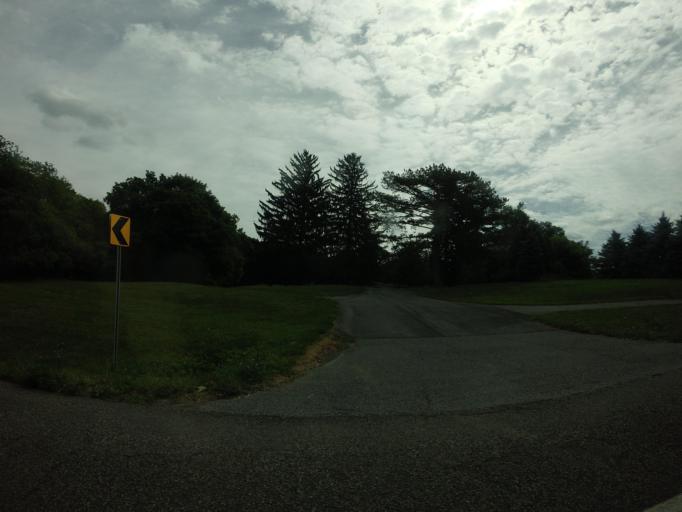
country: US
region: New York
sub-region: Onondaga County
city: Camillus
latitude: 43.0353
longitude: -76.3037
